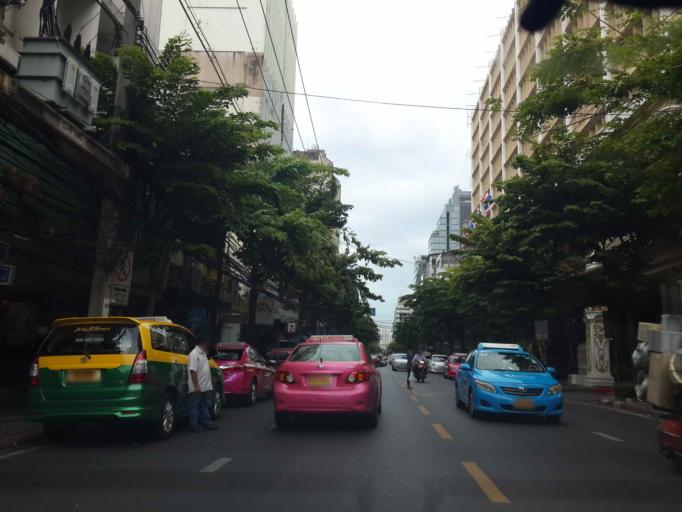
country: TH
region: Bangkok
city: Bang Rak
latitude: 13.7295
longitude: 100.5304
